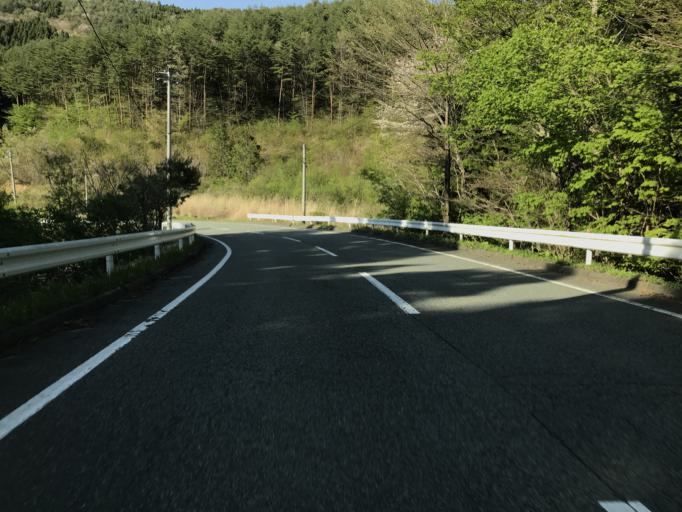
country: JP
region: Fukushima
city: Funehikimachi-funehiki
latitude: 37.5354
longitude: 140.7461
